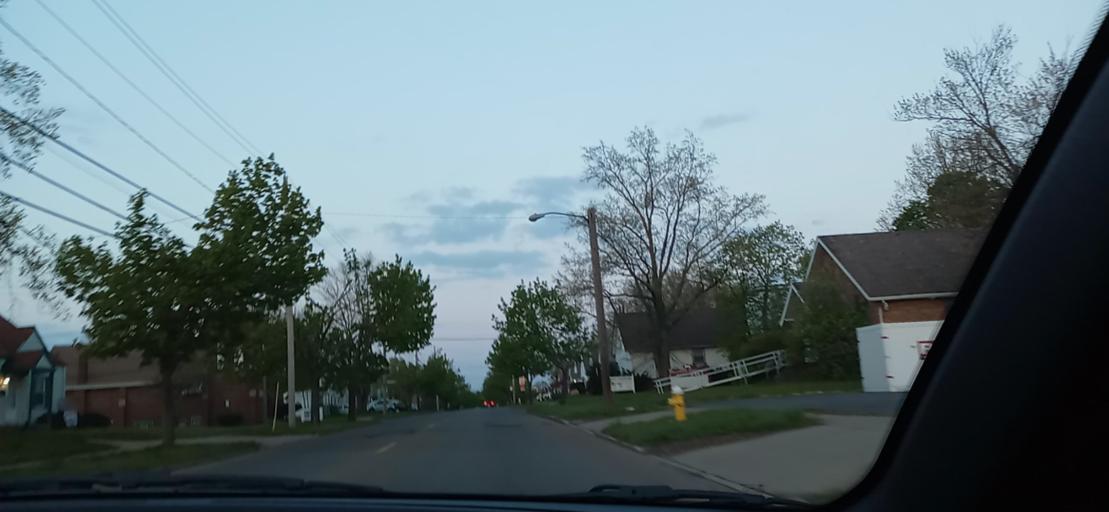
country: US
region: Ohio
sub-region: Summit County
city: Akron
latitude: 41.0469
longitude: -81.4975
